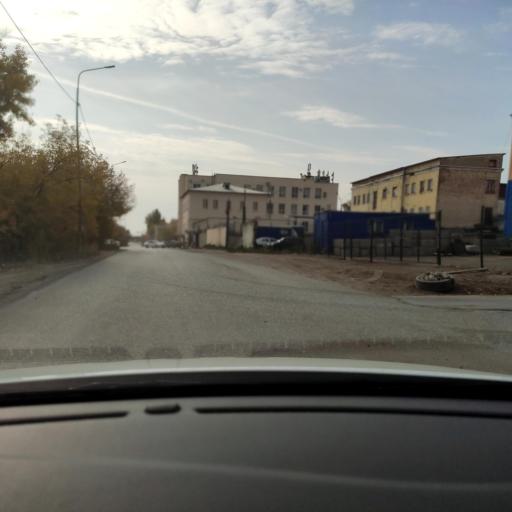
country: RU
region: Tatarstan
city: Verkhniy Uslon
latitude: 55.8012
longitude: 49.0451
